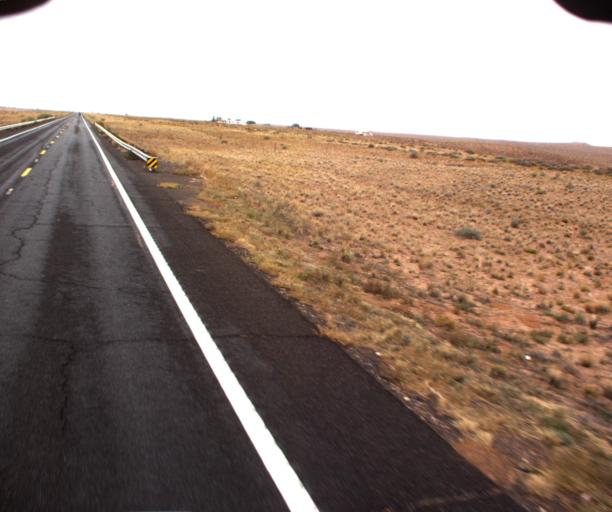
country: US
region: Arizona
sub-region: Coconino County
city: Tuba City
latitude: 36.1557
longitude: -111.1200
